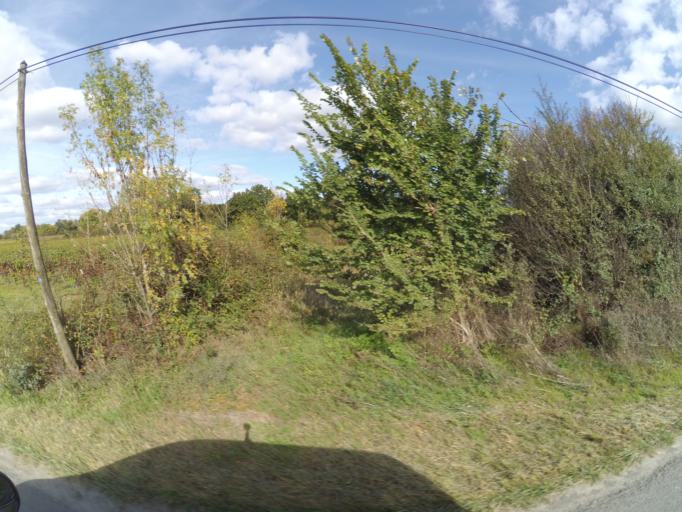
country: FR
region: Pays de la Loire
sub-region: Departement de la Loire-Atlantique
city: Saint-Lumine-de-Clisson
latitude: 47.1050
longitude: -1.3246
